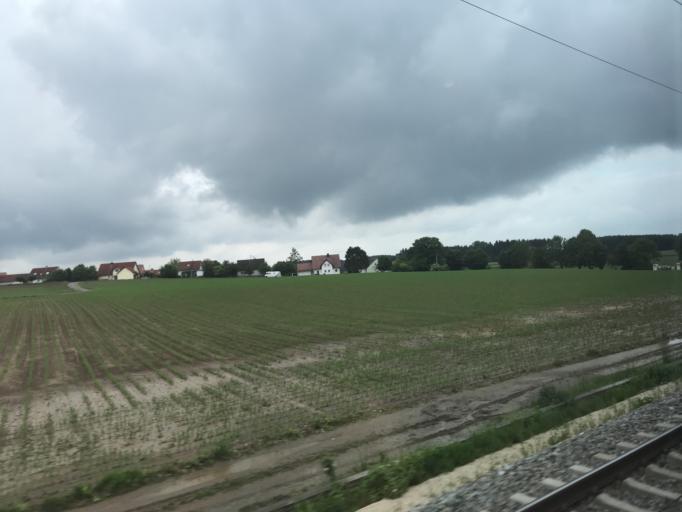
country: DE
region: Bavaria
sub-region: Swabia
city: Kutzenhausen
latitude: 48.3317
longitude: 10.6796
